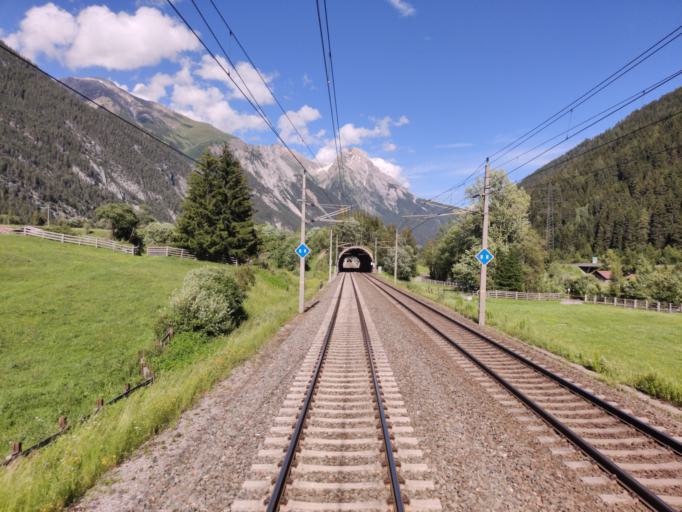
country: AT
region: Tyrol
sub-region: Politischer Bezirk Landeck
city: Flirsch
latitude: 47.1464
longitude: 10.3472
